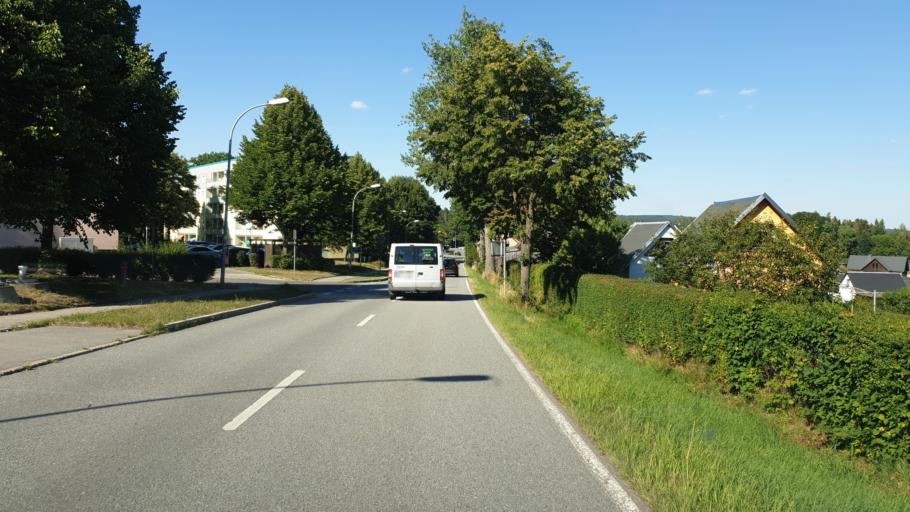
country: DE
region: Saxony
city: Schwarzenberg
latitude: 50.5315
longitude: 12.7701
